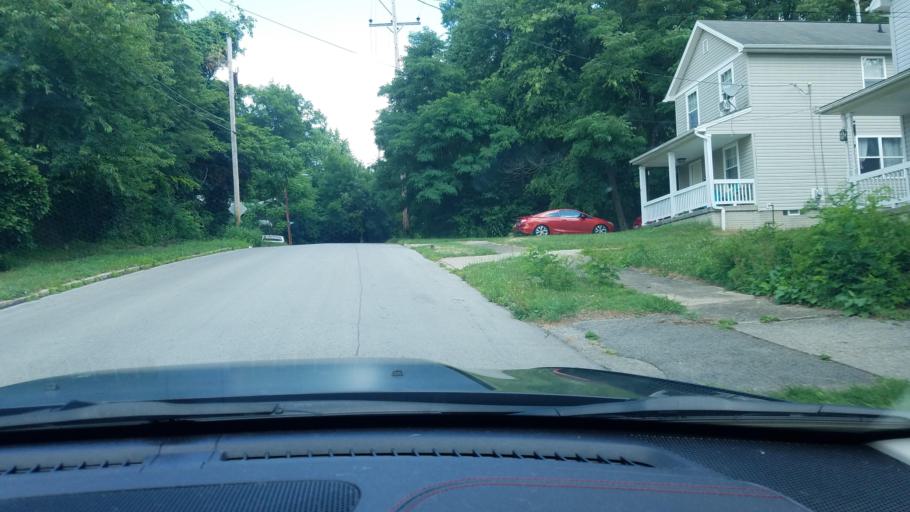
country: US
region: Ohio
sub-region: Mahoning County
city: Campbell
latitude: 41.0770
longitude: -80.6027
